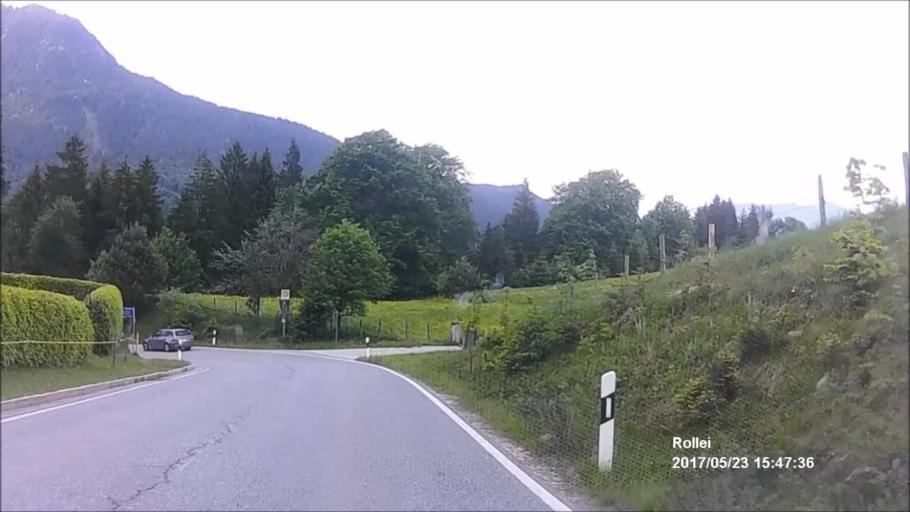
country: DE
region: Bavaria
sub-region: Upper Bavaria
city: Bischofswiesen
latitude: 47.6524
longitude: 12.9455
